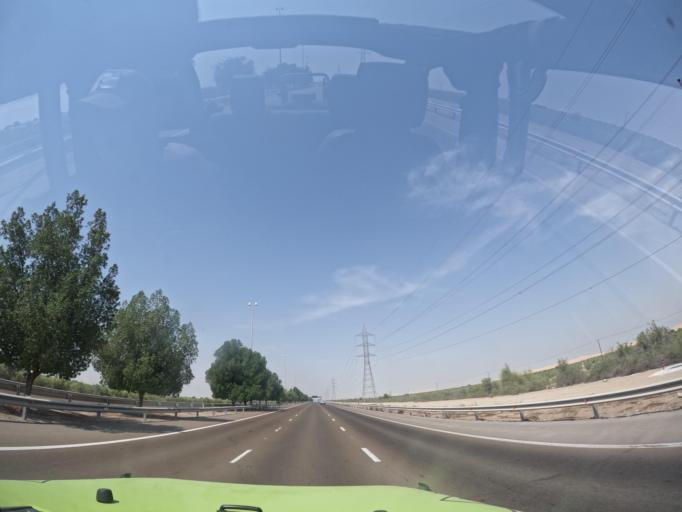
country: AE
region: Abu Dhabi
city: Abu Dhabi
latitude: 24.2155
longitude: 54.8800
